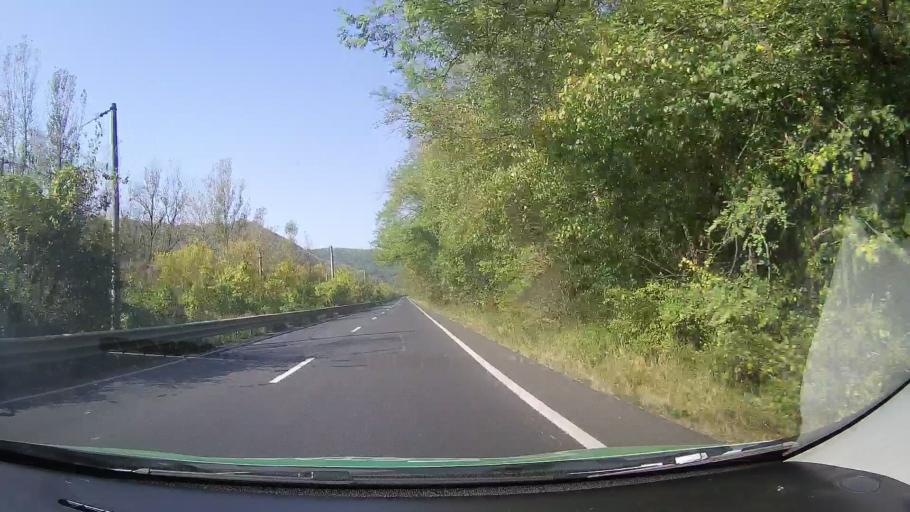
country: RO
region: Hunedoara
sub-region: Comuna Zam
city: Zam
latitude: 45.9743
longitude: 22.4401
